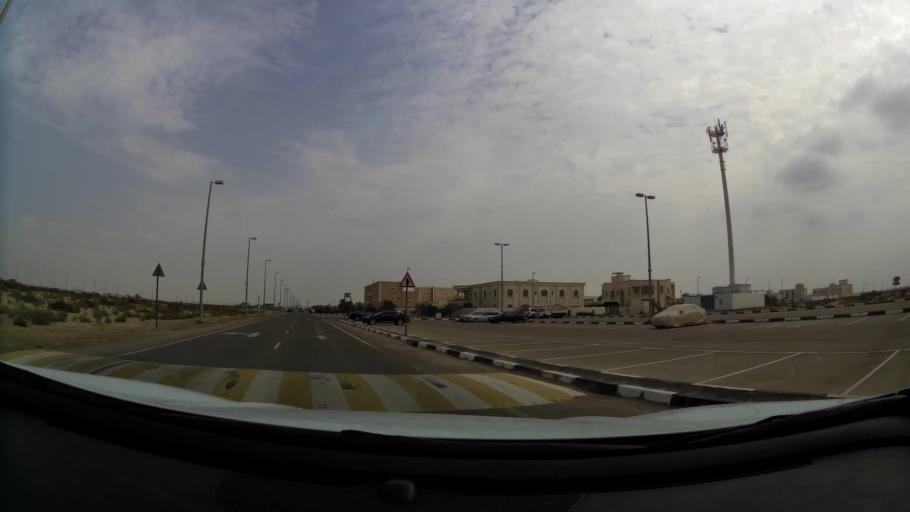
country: AE
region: Abu Dhabi
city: Abu Dhabi
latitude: 24.6502
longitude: 54.6787
